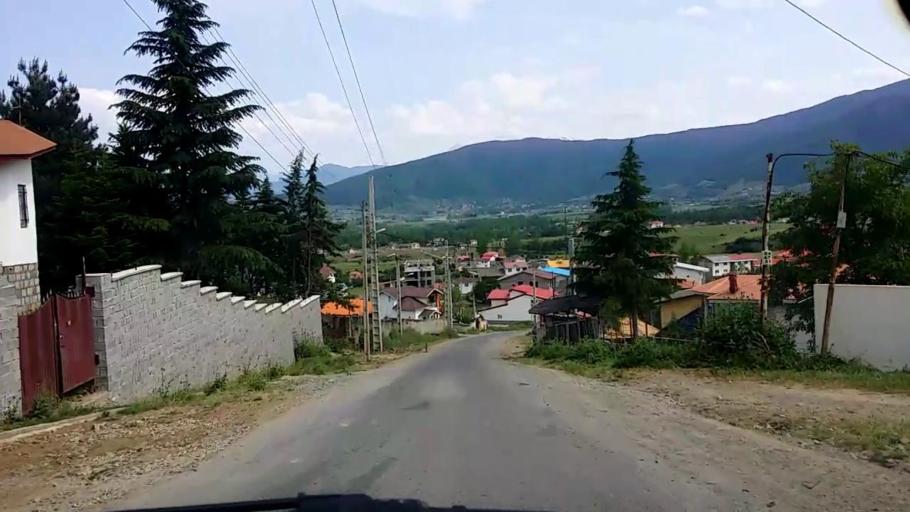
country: IR
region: Mazandaran
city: `Abbasabad
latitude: 36.5497
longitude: 51.1845
